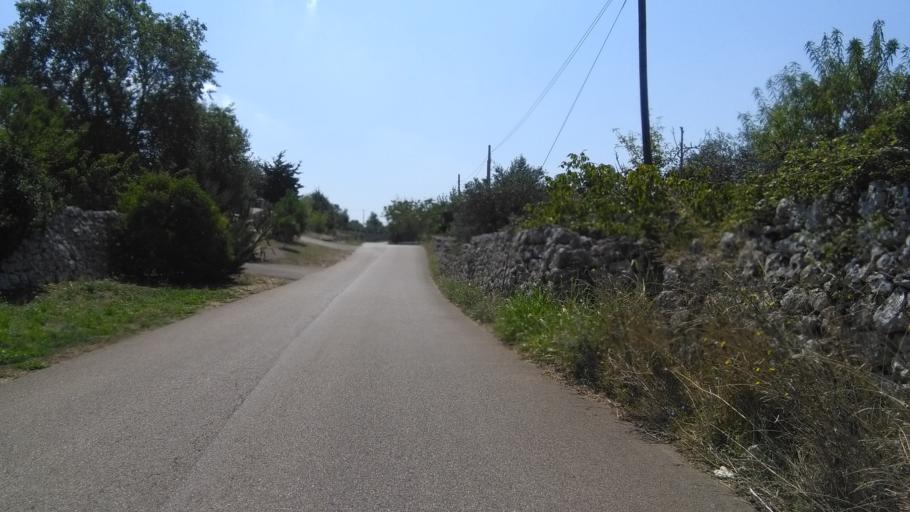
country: IT
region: Apulia
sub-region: Provincia di Bari
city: Putignano
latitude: 40.8296
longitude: 17.1339
